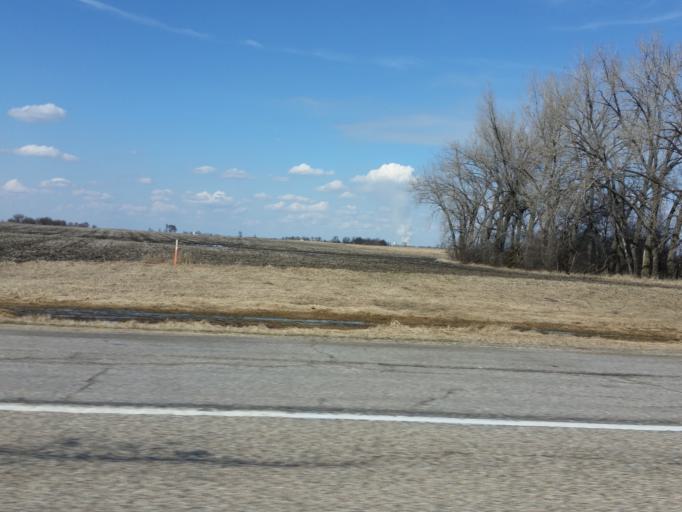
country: US
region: Minnesota
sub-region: Lac qui Parle County
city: Madison
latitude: 44.9360
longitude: -96.4526
